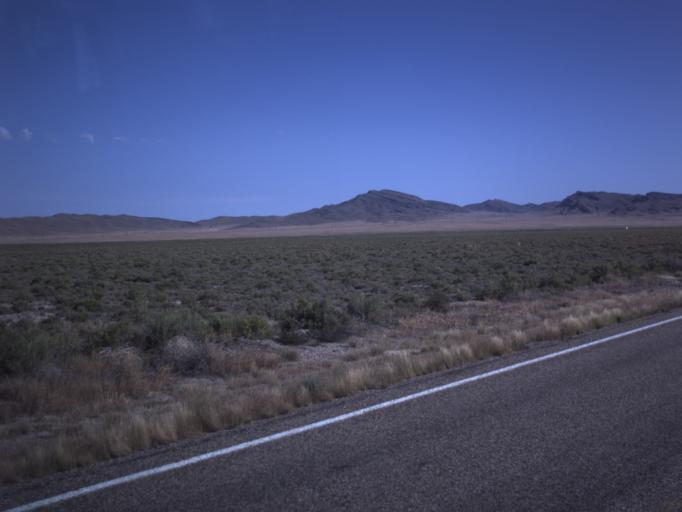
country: US
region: Utah
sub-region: Beaver County
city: Milford
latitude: 38.6955
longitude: -112.9740
